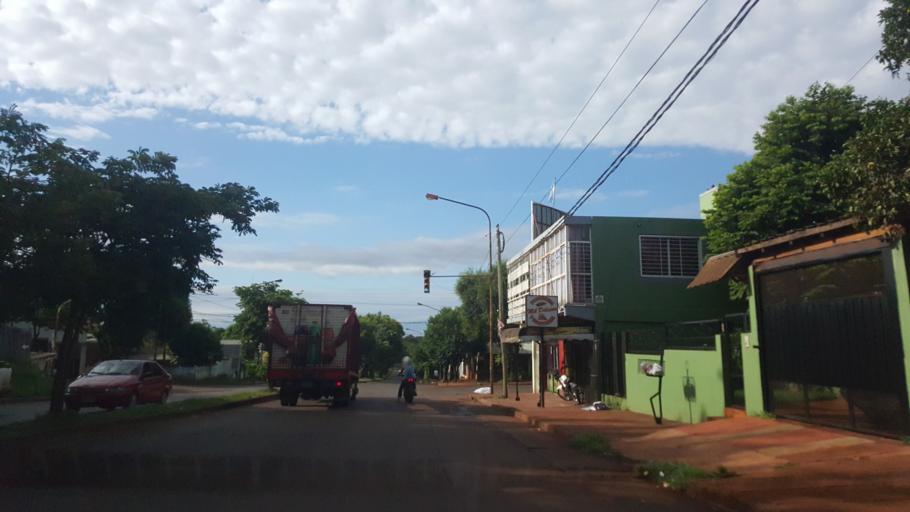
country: AR
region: Misiones
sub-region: Departamento de Capital
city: Posadas
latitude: -27.3844
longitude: -55.9341
